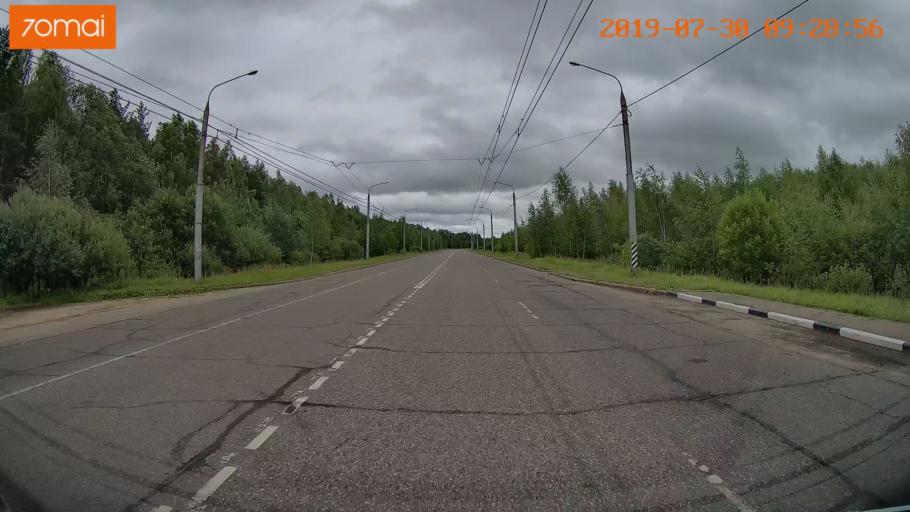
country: RU
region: Ivanovo
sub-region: Gorod Ivanovo
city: Ivanovo
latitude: 56.9490
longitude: 40.9472
